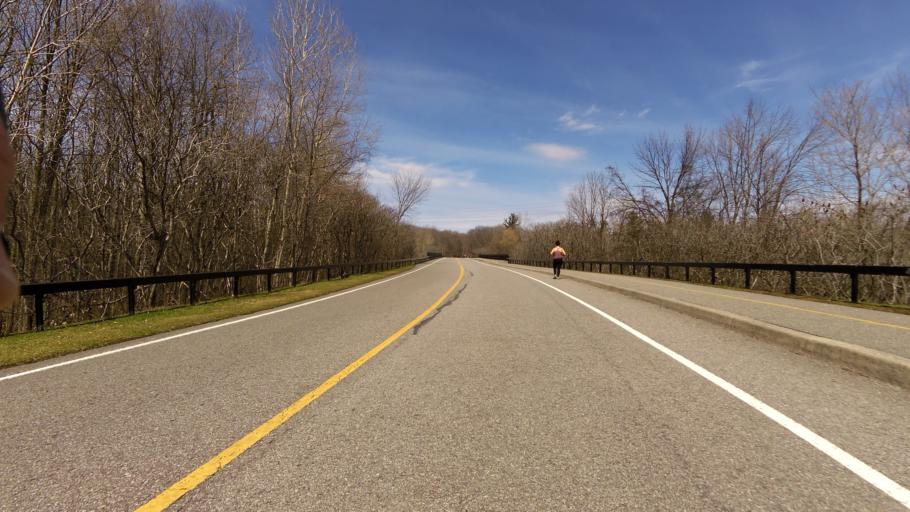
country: CA
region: Quebec
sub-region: Outaouais
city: Gatineau
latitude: 45.4450
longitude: -75.7609
